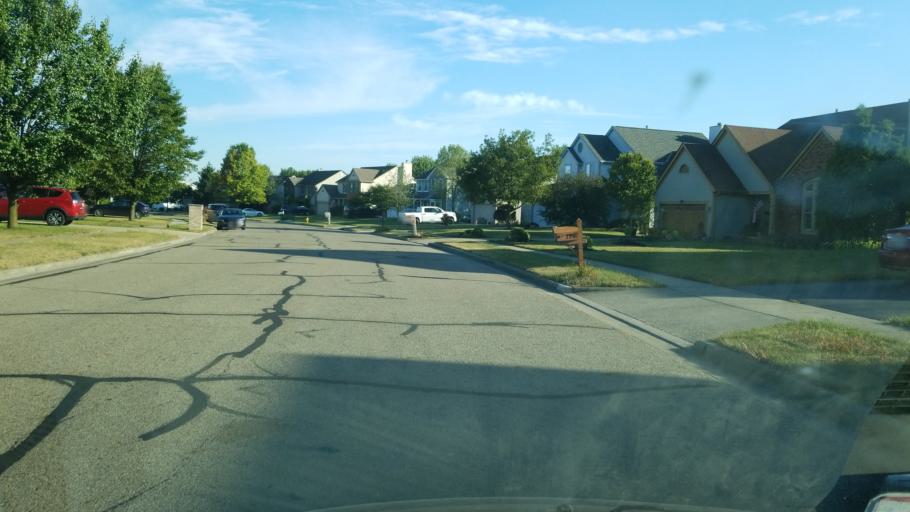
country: US
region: Ohio
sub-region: Delaware County
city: Lewis Center
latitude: 40.1657
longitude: -82.9951
